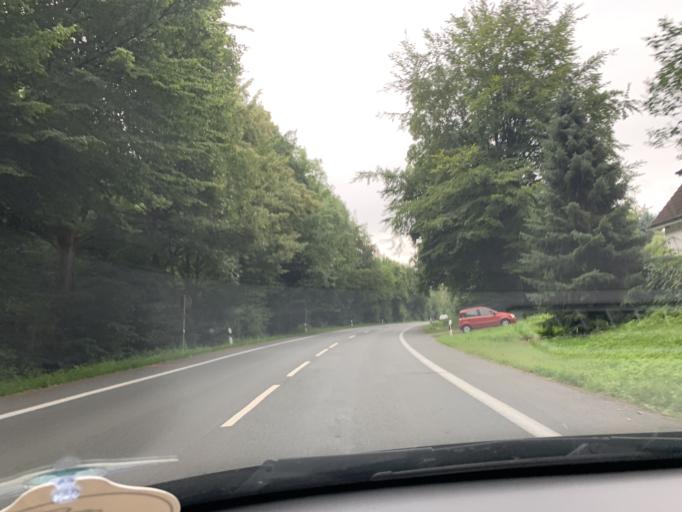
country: DE
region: North Rhine-Westphalia
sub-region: Regierungsbezirk Munster
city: Tecklenburg
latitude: 52.2176
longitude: 7.8240
